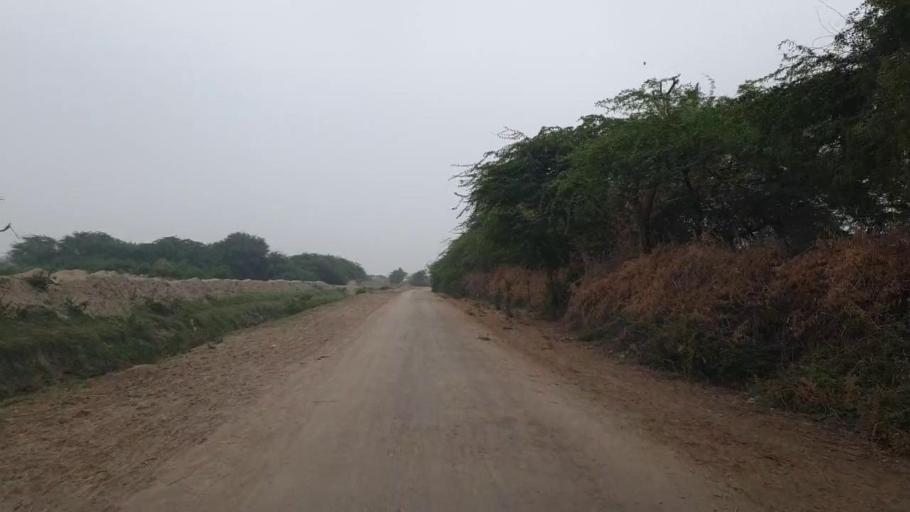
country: PK
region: Sindh
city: Badin
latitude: 24.6013
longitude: 68.6751
